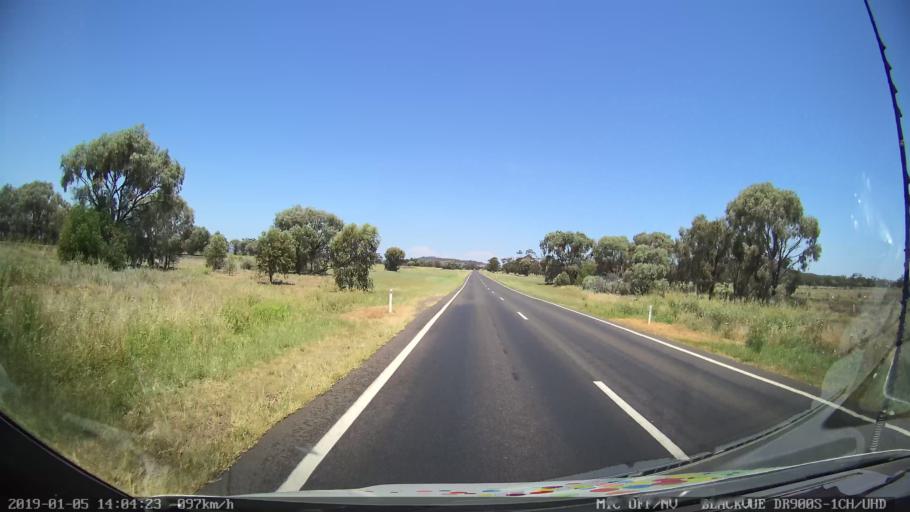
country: AU
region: New South Wales
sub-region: Gunnedah
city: Gunnedah
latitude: -31.1994
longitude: 150.3631
